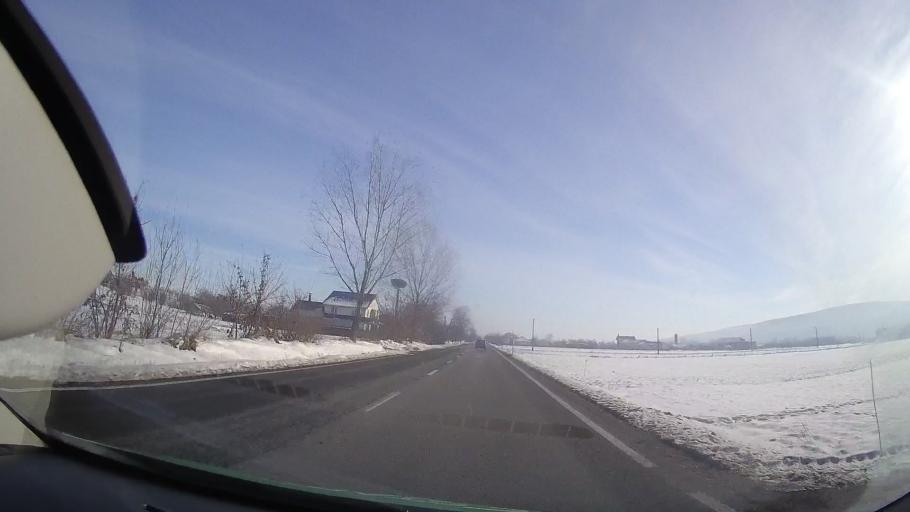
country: RO
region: Neamt
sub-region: Comuna Negresti
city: Negresti
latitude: 47.0639
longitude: 26.3780
